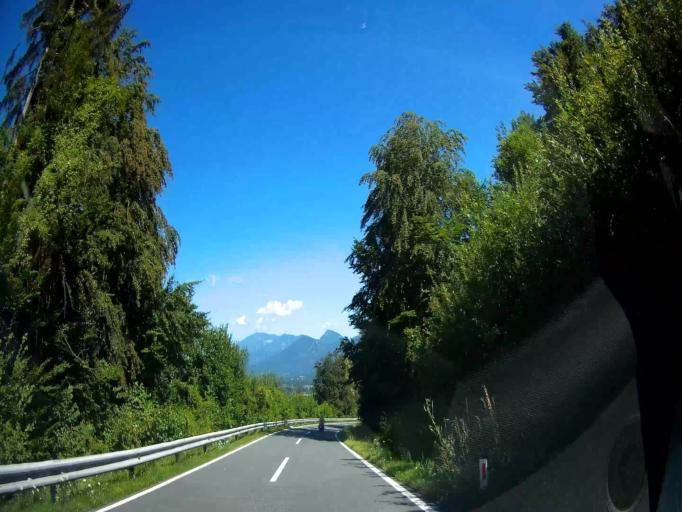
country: AT
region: Carinthia
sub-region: Politischer Bezirk Volkermarkt
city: Gallizien
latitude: 46.5552
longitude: 14.4884
